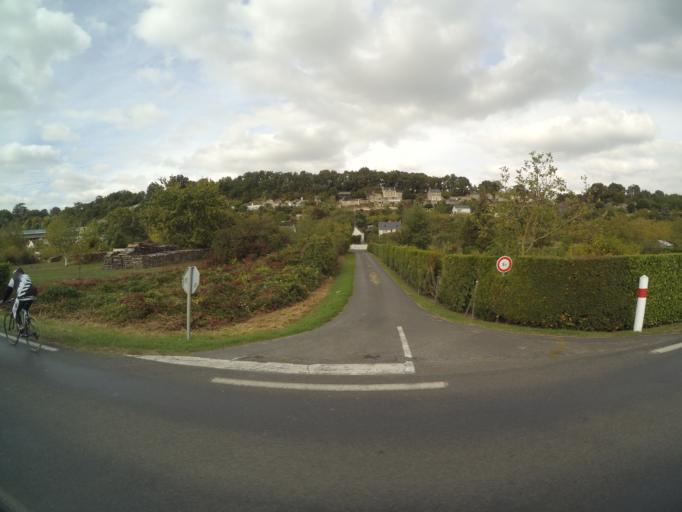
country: FR
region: Centre
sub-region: Departement d'Indre-et-Loire
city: Vernou-sur-Brenne
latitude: 47.4122
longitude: 0.8268
